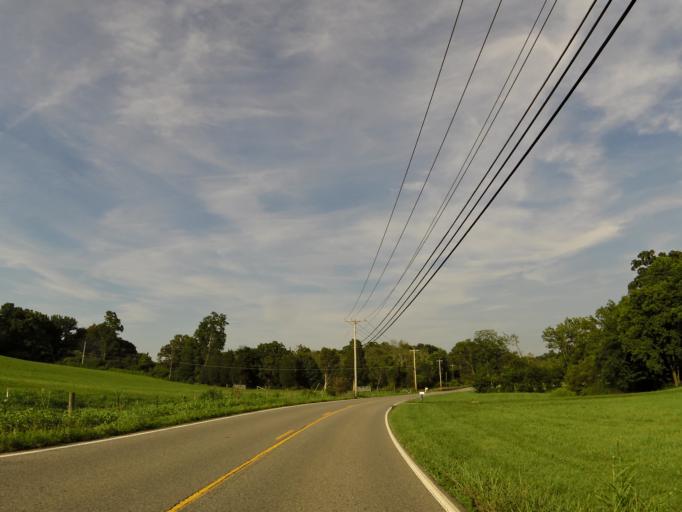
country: US
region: Tennessee
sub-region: Blount County
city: Wildwood
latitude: 35.8290
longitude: -83.8050
